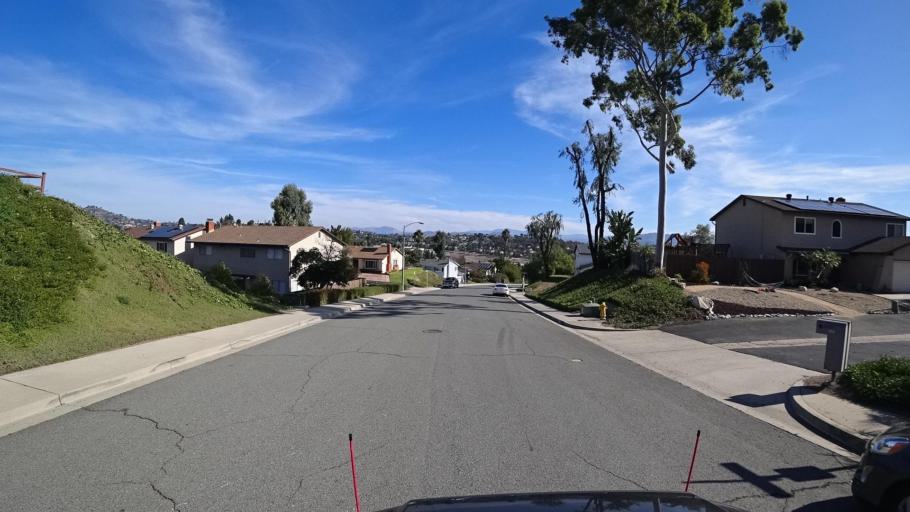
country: US
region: California
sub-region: San Diego County
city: Spring Valley
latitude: 32.7300
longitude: -116.9804
